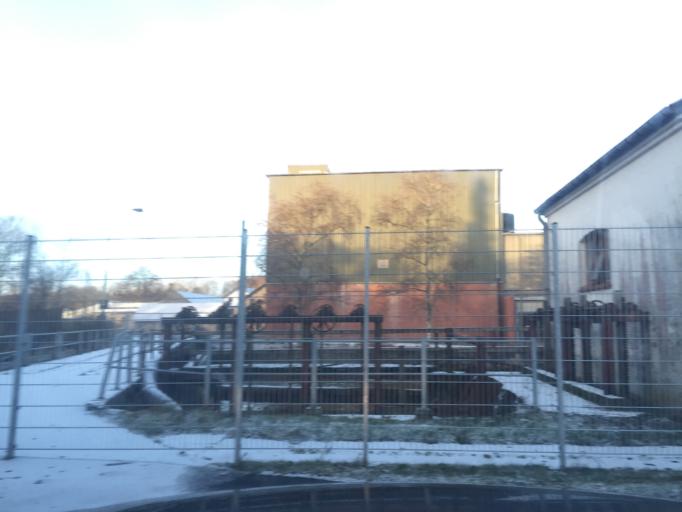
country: DK
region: South Denmark
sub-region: Odense Kommune
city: Odense
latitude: 55.3620
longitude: 10.3793
